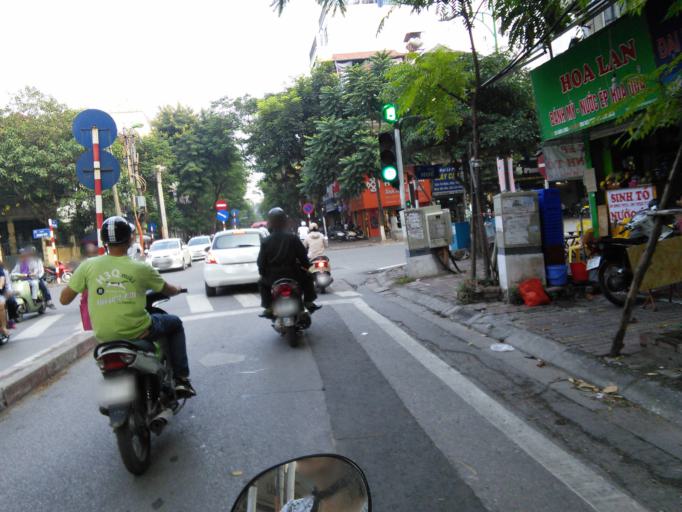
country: VN
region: Ha Noi
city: Hai BaTrung
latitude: 21.0198
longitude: 105.8517
